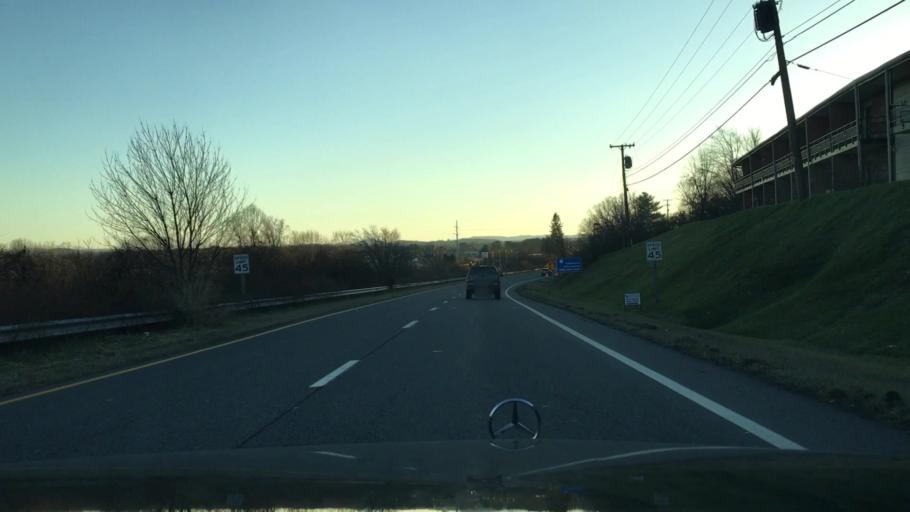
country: US
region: Virginia
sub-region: Montgomery County
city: Merrimac
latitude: 37.1828
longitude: -80.4106
